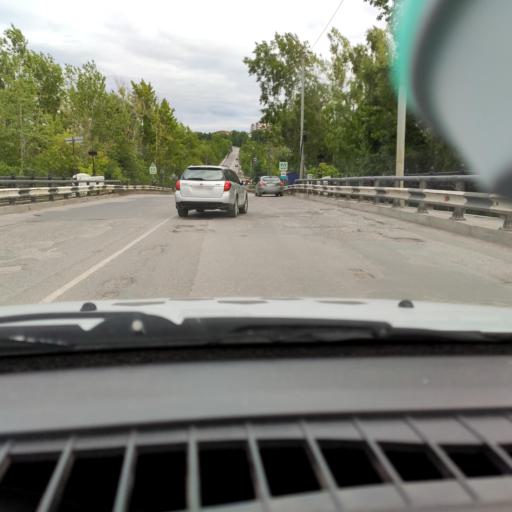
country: RU
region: Perm
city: Chusovoy
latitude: 58.2852
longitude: 57.8127
